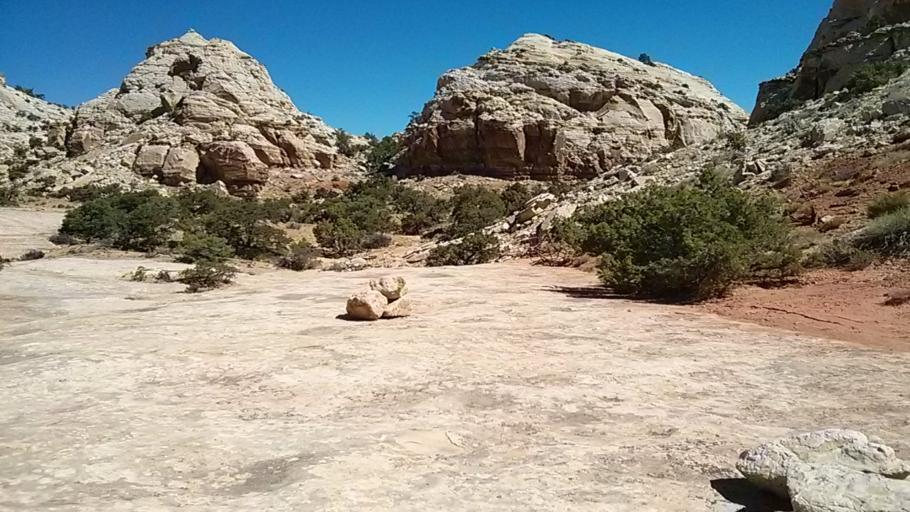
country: US
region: Utah
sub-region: Wayne County
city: Loa
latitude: 38.3048
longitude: -111.2574
